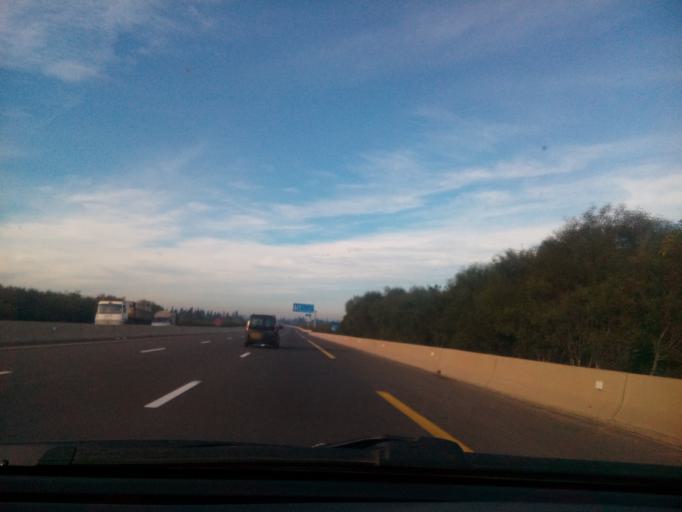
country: DZ
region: Mascara
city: Mascara
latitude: 35.6222
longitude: 0.0585
